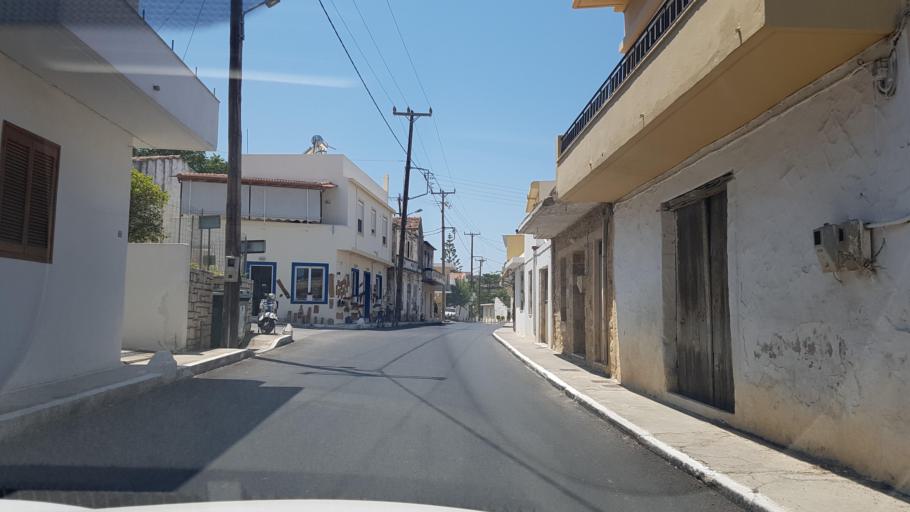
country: GR
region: Crete
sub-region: Nomos Rethymnis
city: Rethymno
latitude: 35.3574
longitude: 24.5613
